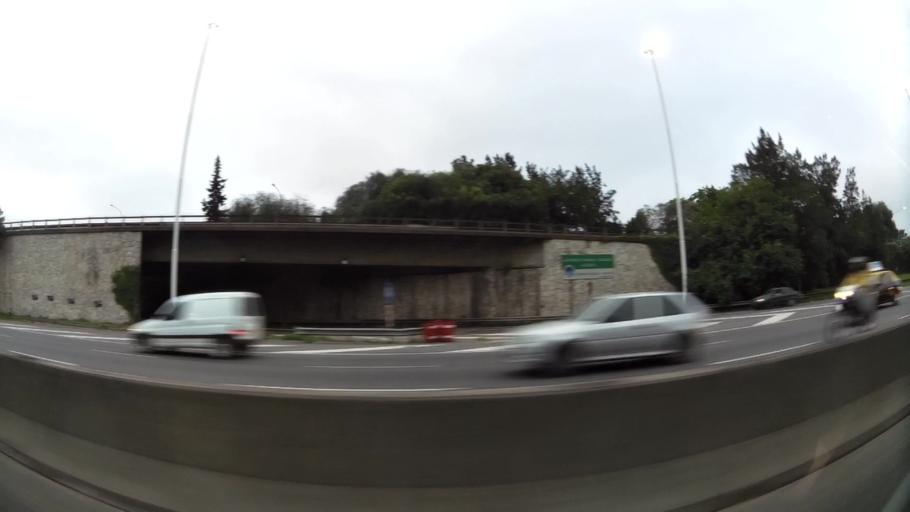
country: AR
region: Buenos Aires
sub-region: Partido de Vicente Lopez
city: Olivos
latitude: -34.5449
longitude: -58.4892
